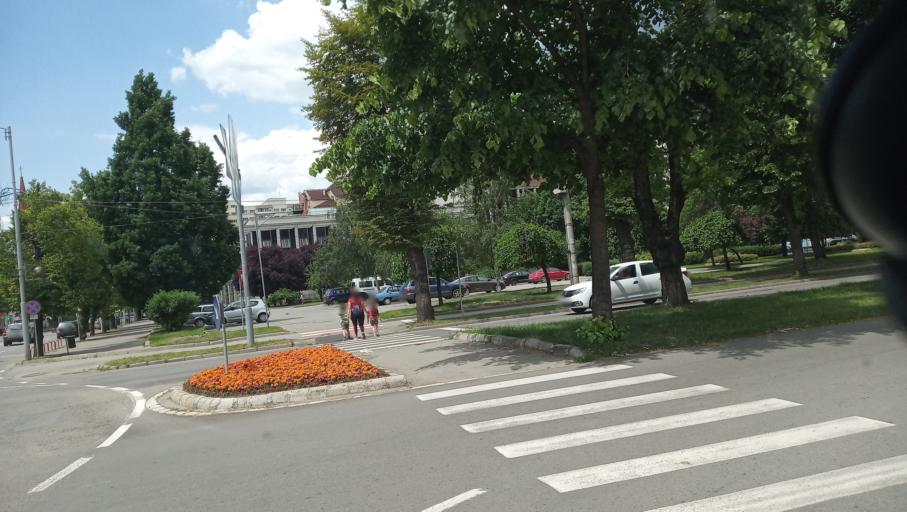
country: RO
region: Bistrita-Nasaud
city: Bistrita
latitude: 47.1311
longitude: 24.4900
